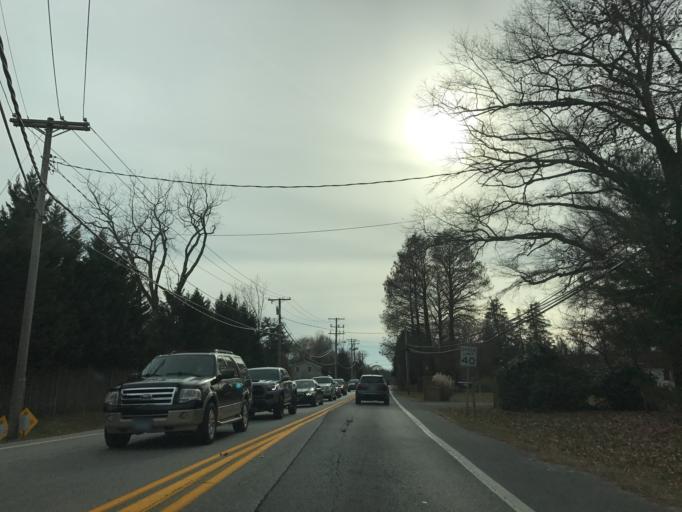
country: US
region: Maryland
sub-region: Anne Arundel County
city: Severna Park
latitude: 39.0930
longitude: -76.5481
